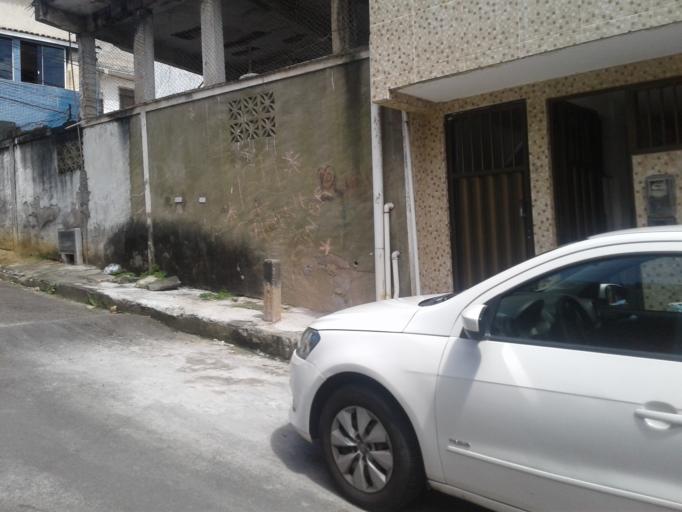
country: BR
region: Bahia
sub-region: Salvador
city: Salvador
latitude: -12.9119
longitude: -38.4700
